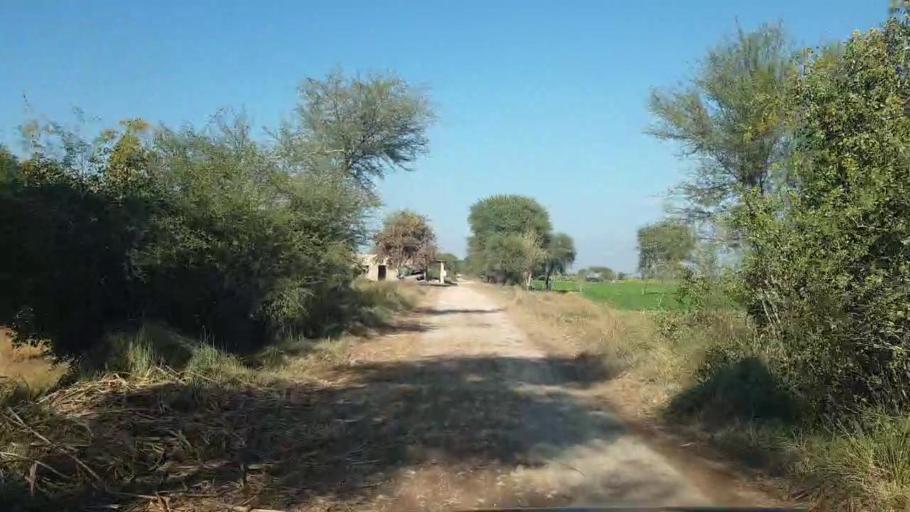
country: PK
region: Sindh
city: Shahdadpur
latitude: 25.9350
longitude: 68.5244
